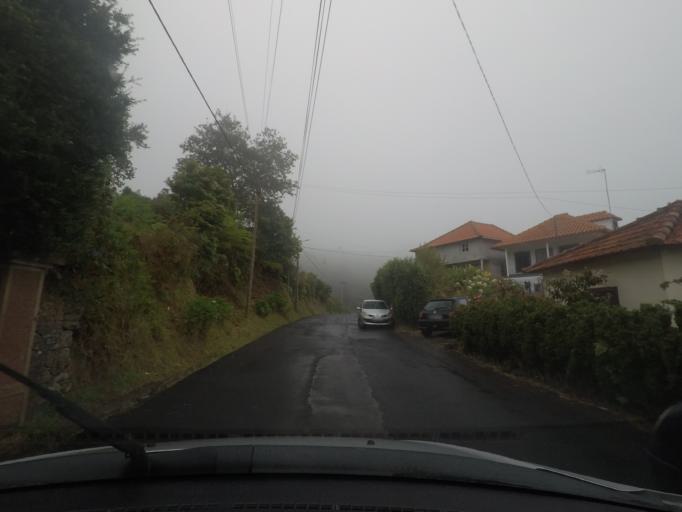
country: PT
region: Madeira
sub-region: Santana
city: Santana
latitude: 32.7949
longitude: -16.8767
